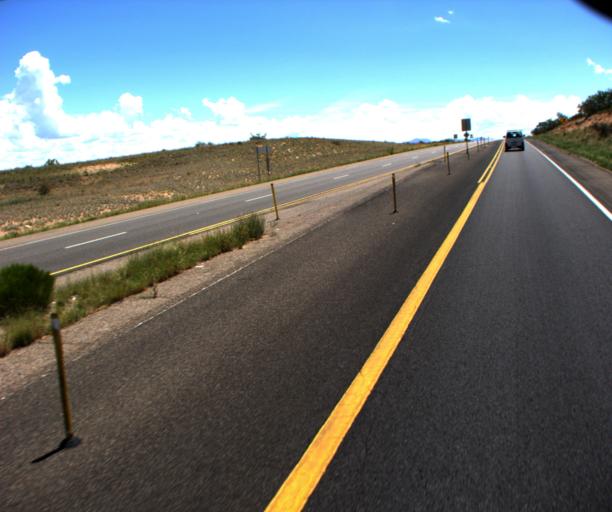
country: US
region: Arizona
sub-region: Yavapai County
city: Verde Village
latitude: 34.6634
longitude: -111.9670
